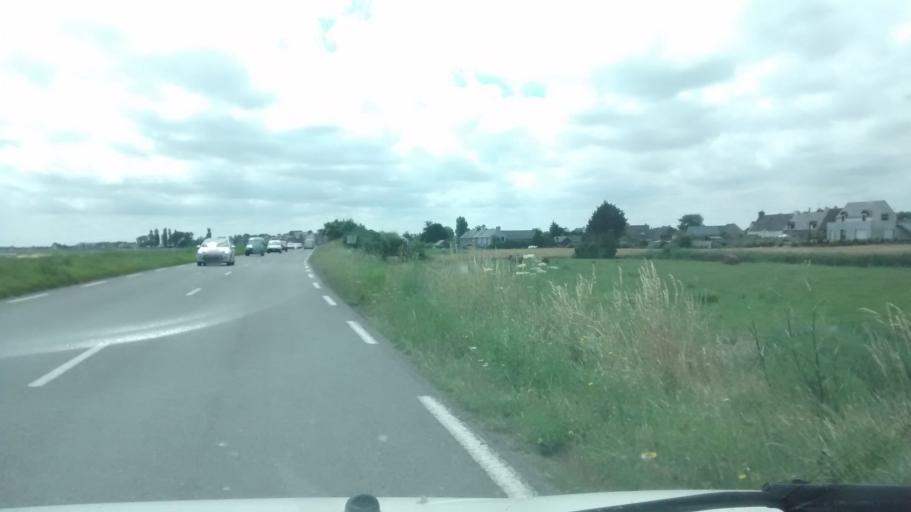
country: FR
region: Brittany
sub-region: Departement d'Ille-et-Vilaine
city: La Fresnais
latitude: 48.6269
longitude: -1.8601
